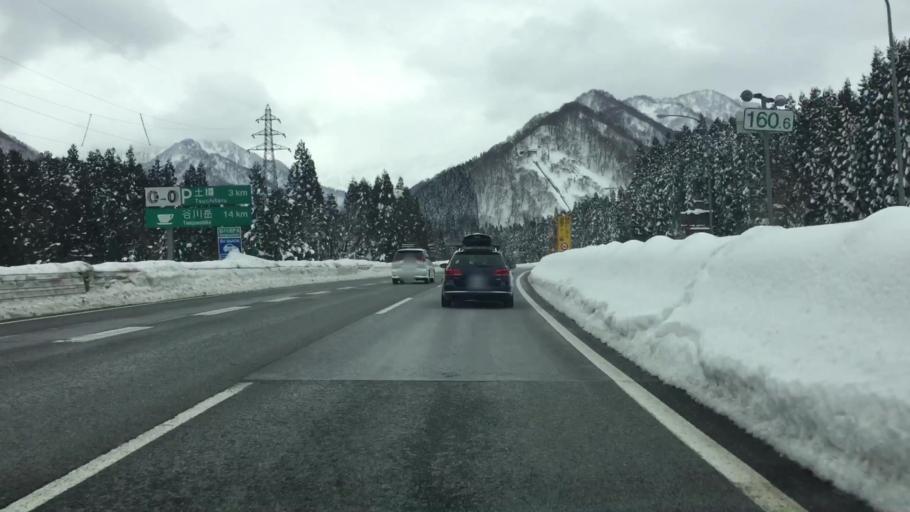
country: JP
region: Niigata
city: Shiozawa
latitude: 36.8847
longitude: 138.8516
